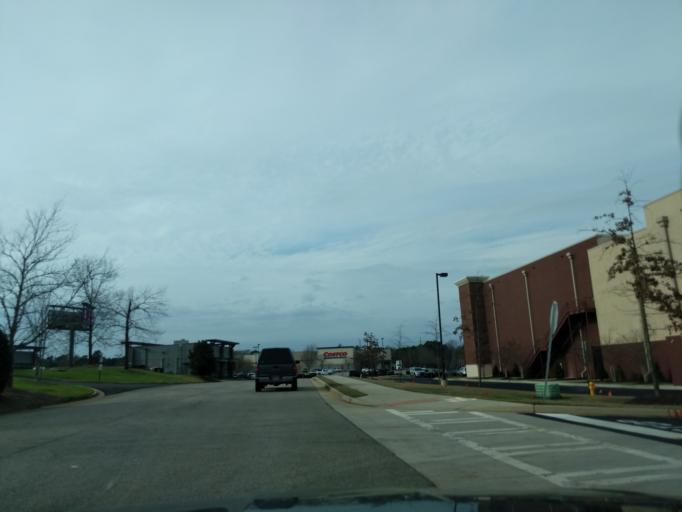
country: US
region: South Carolina
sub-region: Aiken County
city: North Augusta
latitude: 33.5236
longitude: -82.0175
